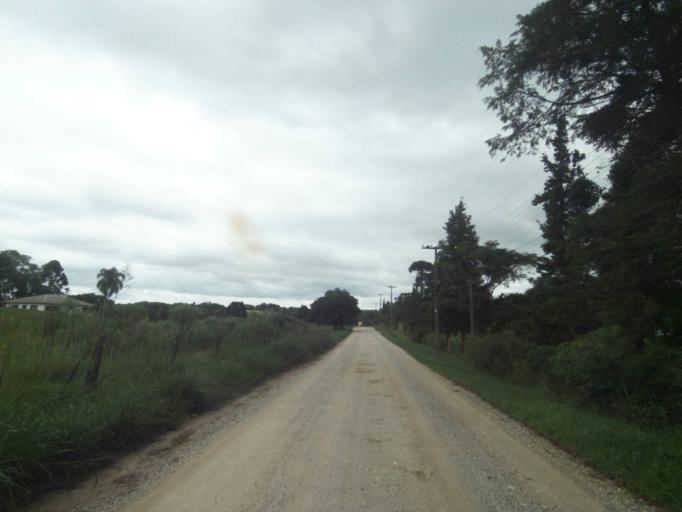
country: BR
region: Parana
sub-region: Quatro Barras
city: Quatro Barras
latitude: -25.3267
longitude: -49.0908
